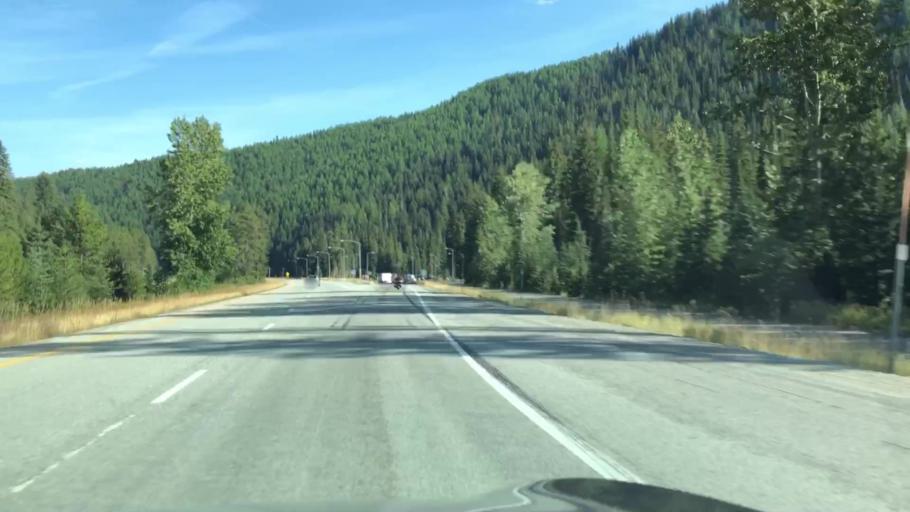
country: US
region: Idaho
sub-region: Shoshone County
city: Wallace
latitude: 47.4217
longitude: -115.6328
